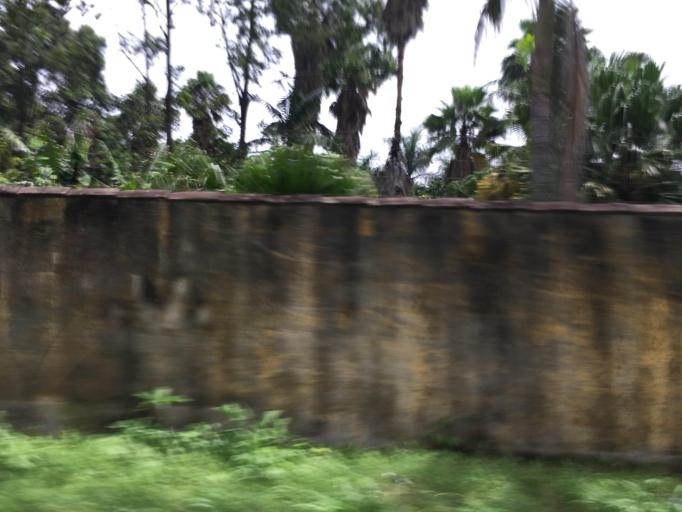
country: GT
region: Guatemala
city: Villa Canales
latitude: 14.4284
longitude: -90.5564
